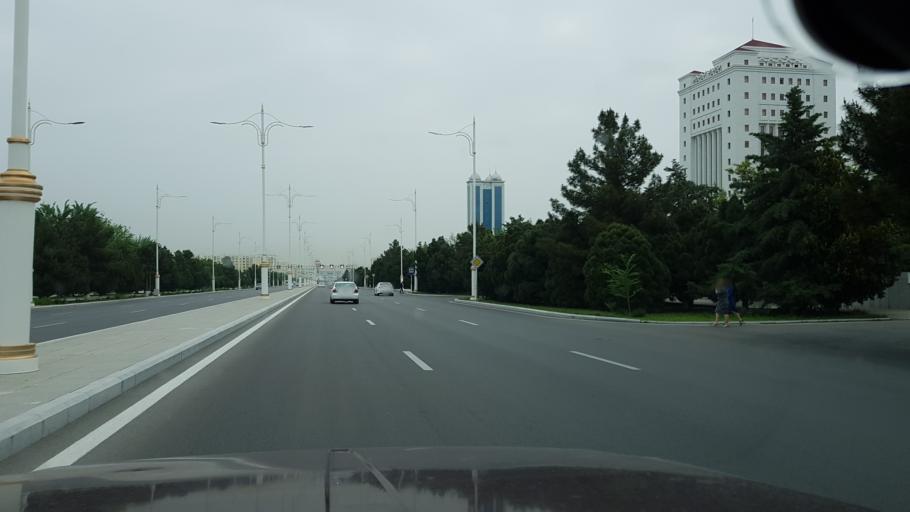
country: TM
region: Ahal
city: Ashgabat
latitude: 37.8890
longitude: 58.3879
